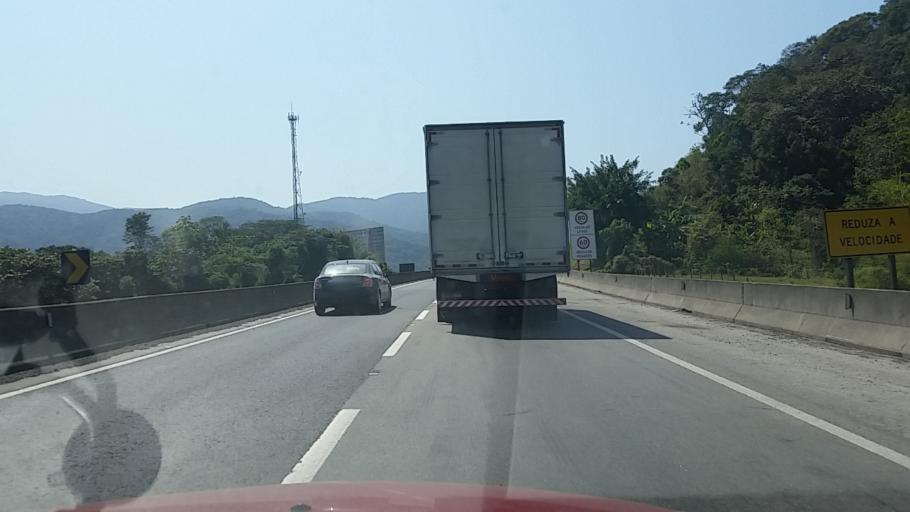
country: BR
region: Sao Paulo
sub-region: Miracatu
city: Miracatu
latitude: -24.1543
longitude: -47.3238
